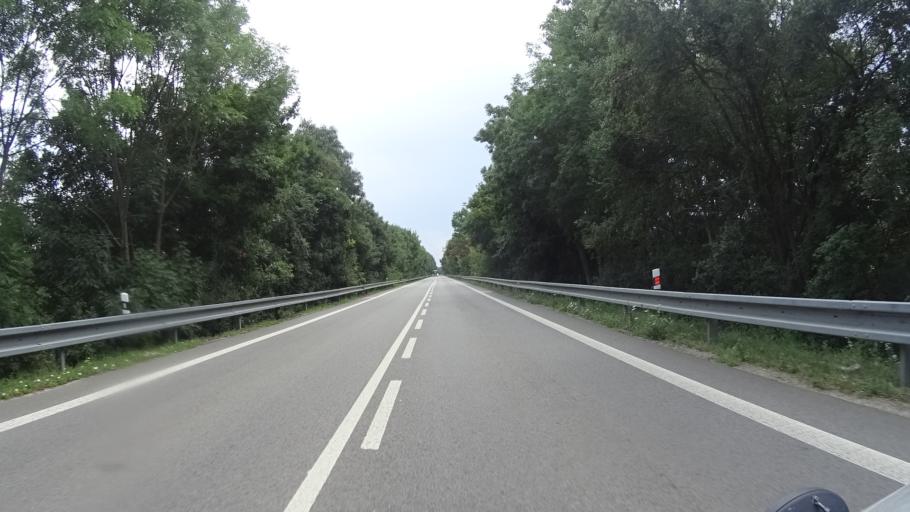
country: CZ
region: South Moravian
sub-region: Okres Breclav
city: Lednice
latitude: 48.8182
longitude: 16.8148
